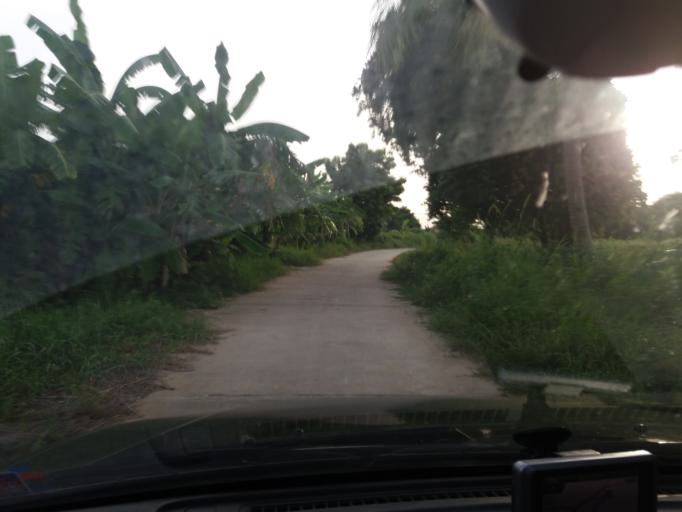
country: TH
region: Suphan Buri
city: Doembang Nangbuat
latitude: 14.8115
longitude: 100.1429
